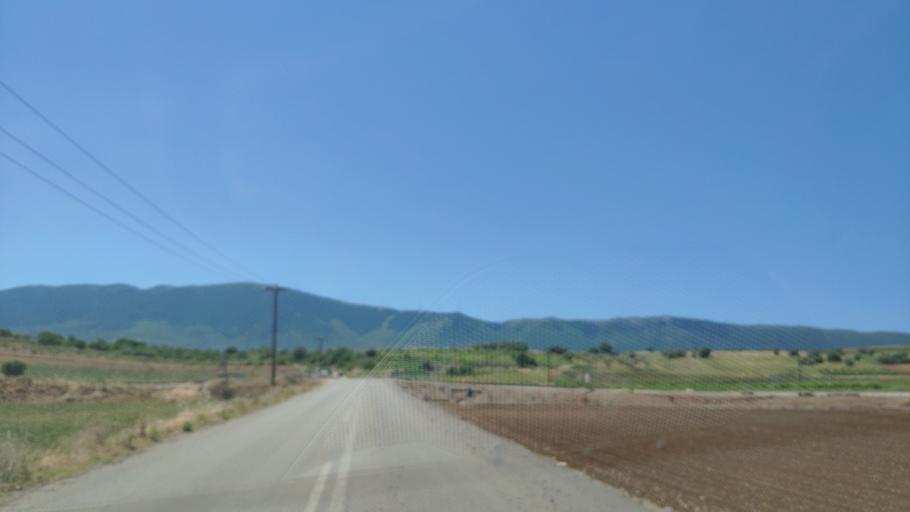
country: GR
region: Central Greece
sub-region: Nomos Voiotias
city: Kaparellion
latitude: 38.2522
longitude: 23.2352
